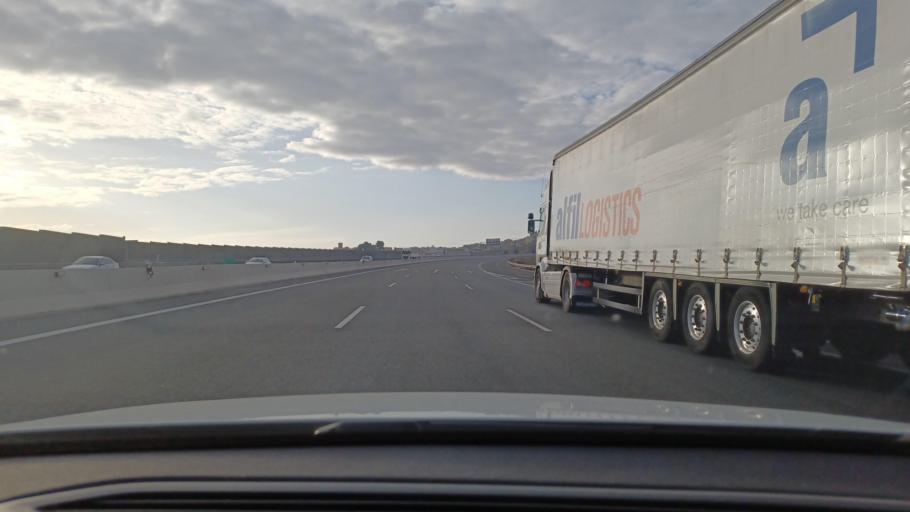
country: ES
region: Valencia
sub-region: Provincia de Valencia
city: La Font de la Figuera
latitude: 38.8143
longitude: -0.8874
